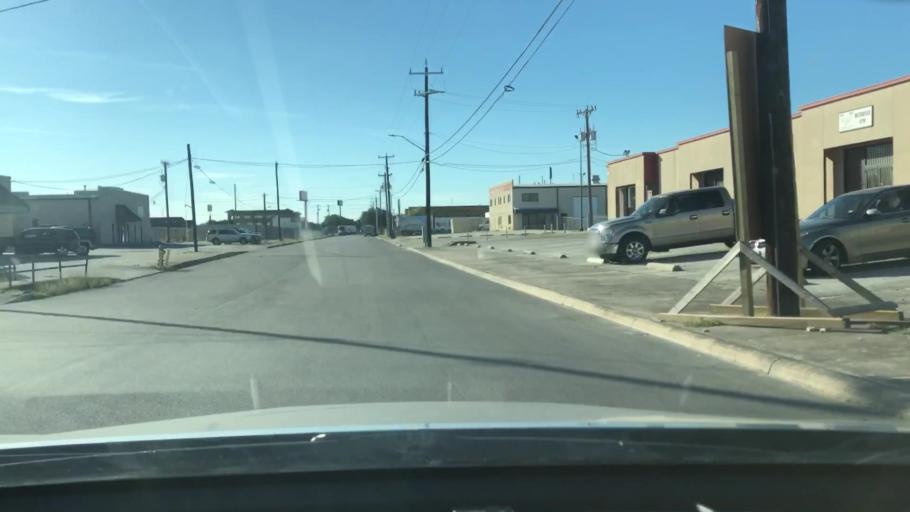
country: US
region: Texas
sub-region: Bexar County
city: Kirby
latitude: 29.4881
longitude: -98.3977
